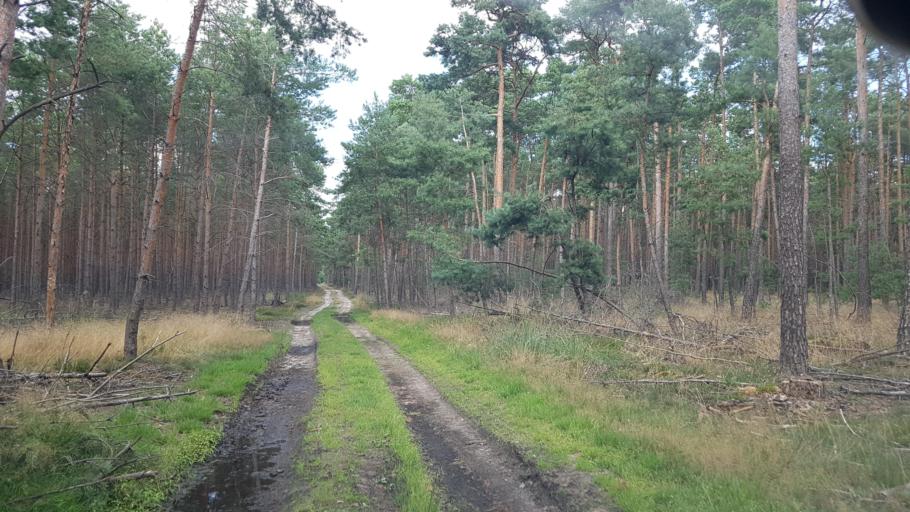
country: DE
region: Brandenburg
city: Trobitz
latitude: 51.6428
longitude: 13.4318
